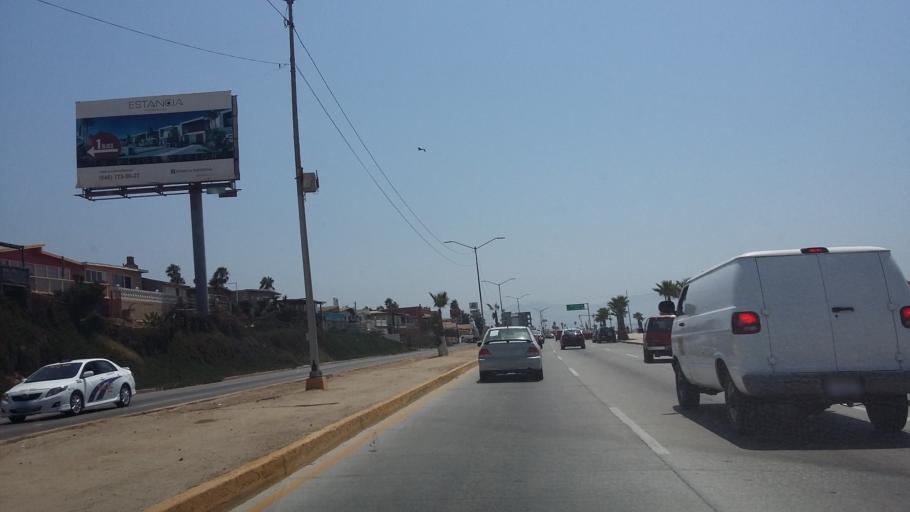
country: MX
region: Baja California
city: Ensenada
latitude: 31.8426
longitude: -116.6115
